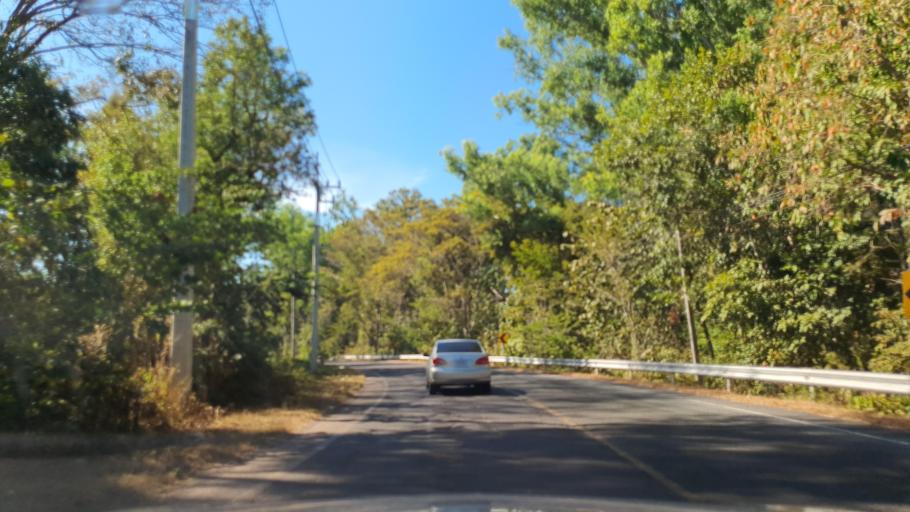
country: TH
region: Kalasin
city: Khao Wong
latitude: 16.7641
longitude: 104.1457
